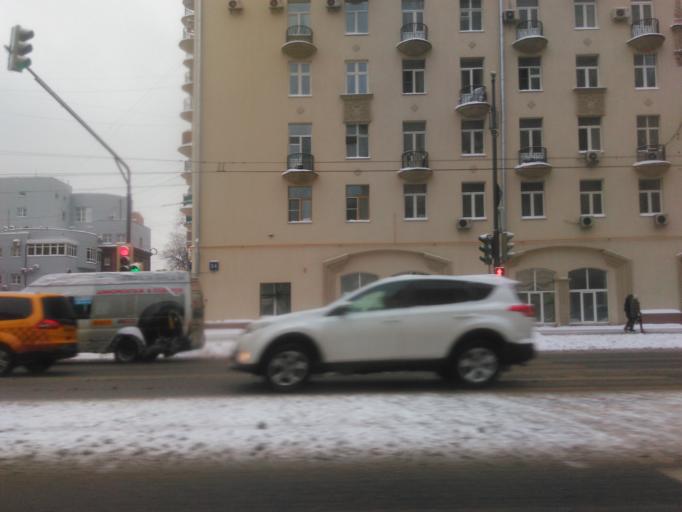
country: RU
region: Moscow
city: Mar'ina Roshcha
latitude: 55.7837
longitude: 37.6348
